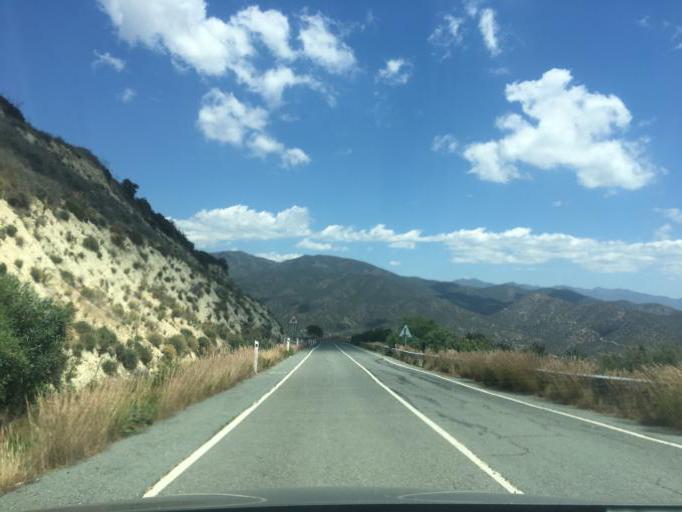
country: CY
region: Limassol
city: Mouttagiaka
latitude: 34.7581
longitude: 33.0636
